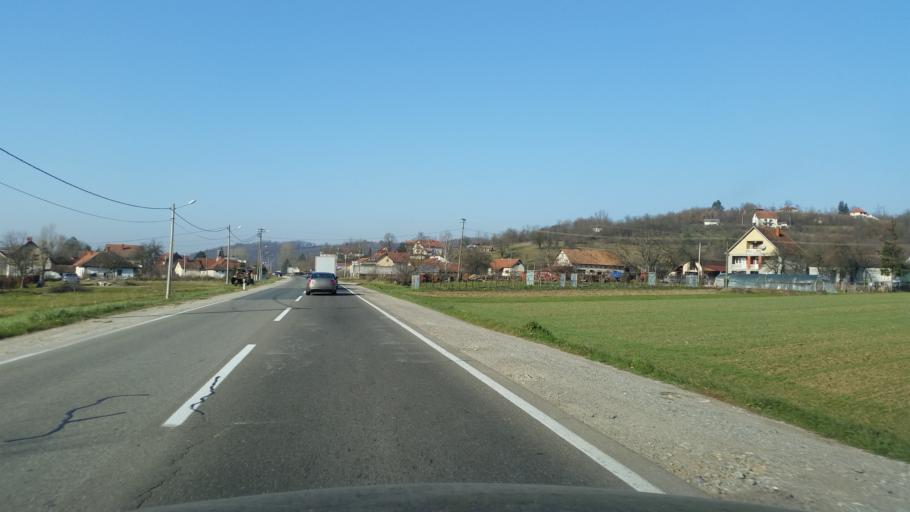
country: RS
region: Central Serbia
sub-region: Kolubarski Okrug
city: Lajkovac
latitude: 44.3339
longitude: 20.2156
